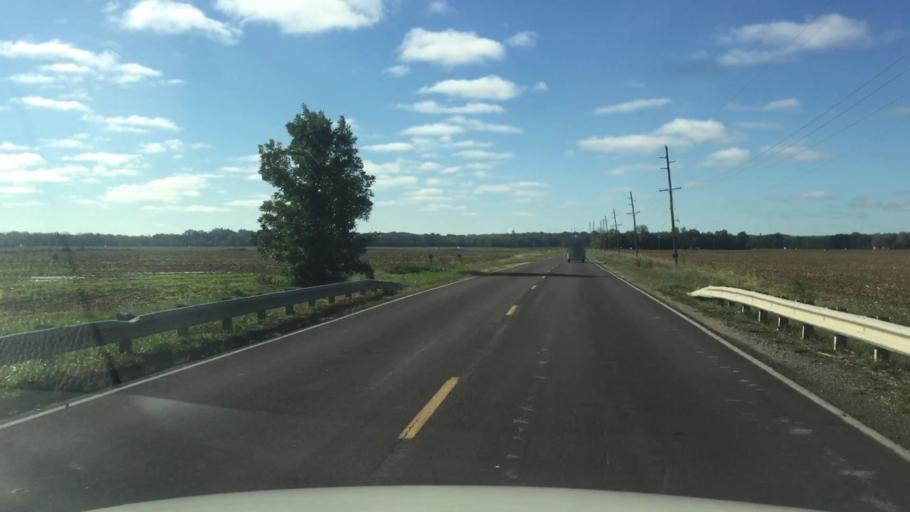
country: US
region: Missouri
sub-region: Howard County
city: New Franklin
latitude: 39.0060
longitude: -92.7383
